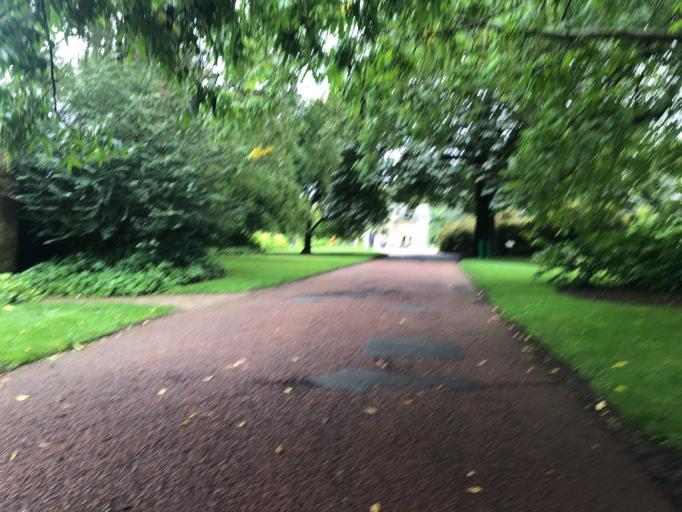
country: GB
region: Scotland
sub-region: Edinburgh
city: Edinburgh
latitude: 55.9655
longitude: -3.2047
